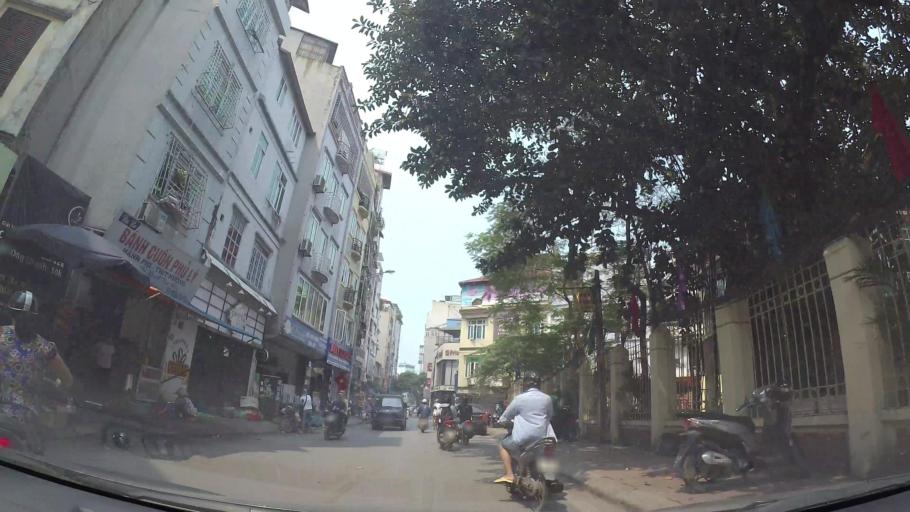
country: VN
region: Ha Noi
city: Dong Da
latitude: 21.0277
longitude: 105.8295
